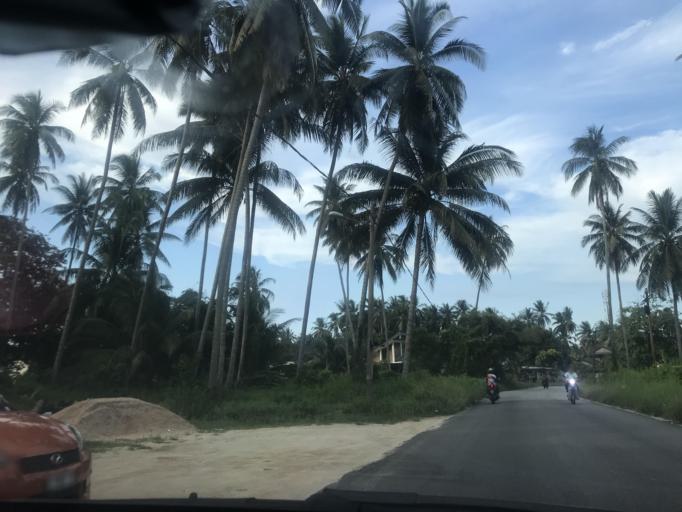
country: MY
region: Kelantan
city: Kota Bharu
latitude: 6.1303
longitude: 102.3622
